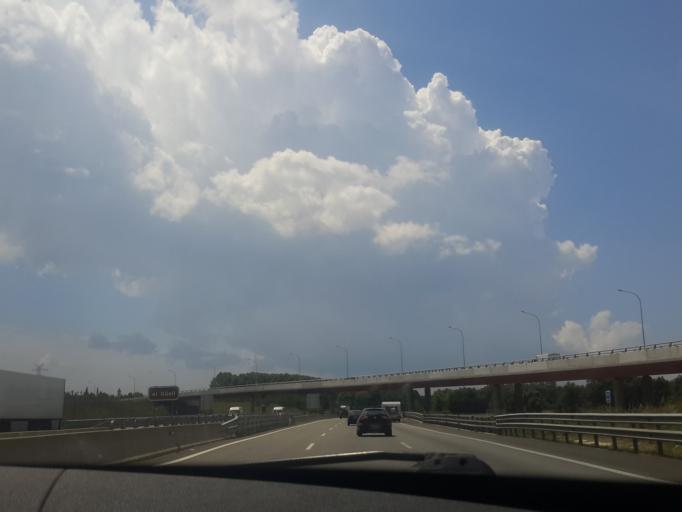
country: ES
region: Catalonia
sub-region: Provincia de Girona
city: Fornells de la Selva
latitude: 41.9347
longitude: 2.7871
